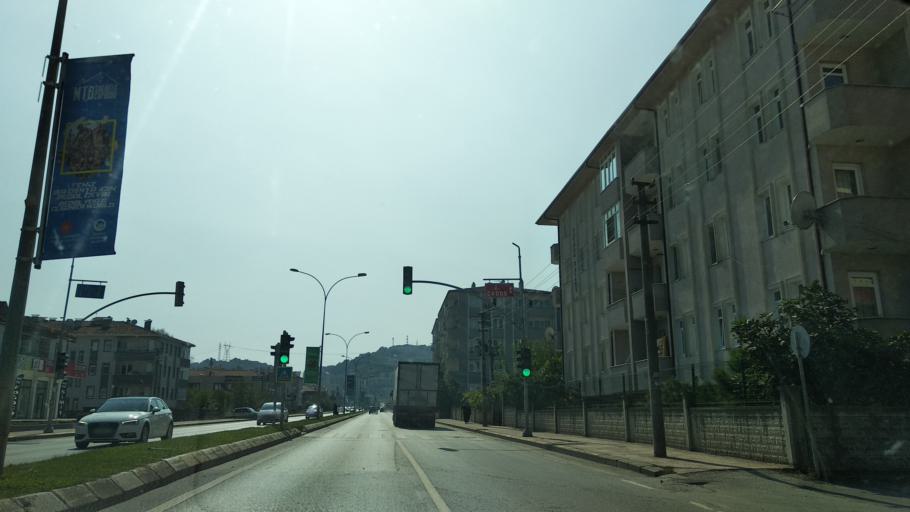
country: TR
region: Sakarya
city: Adapazari
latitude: 40.7656
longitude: 30.3636
